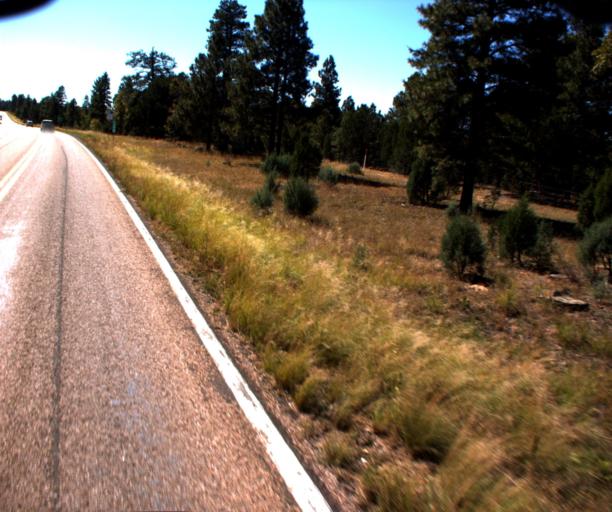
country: US
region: Arizona
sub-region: Navajo County
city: Heber-Overgaard
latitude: 34.3945
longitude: -110.6714
